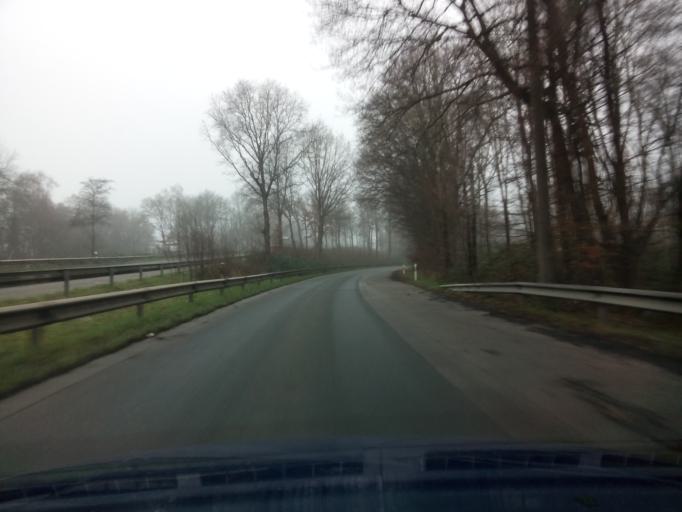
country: DE
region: Bremen
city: Bremen
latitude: 53.1114
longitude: 8.8136
